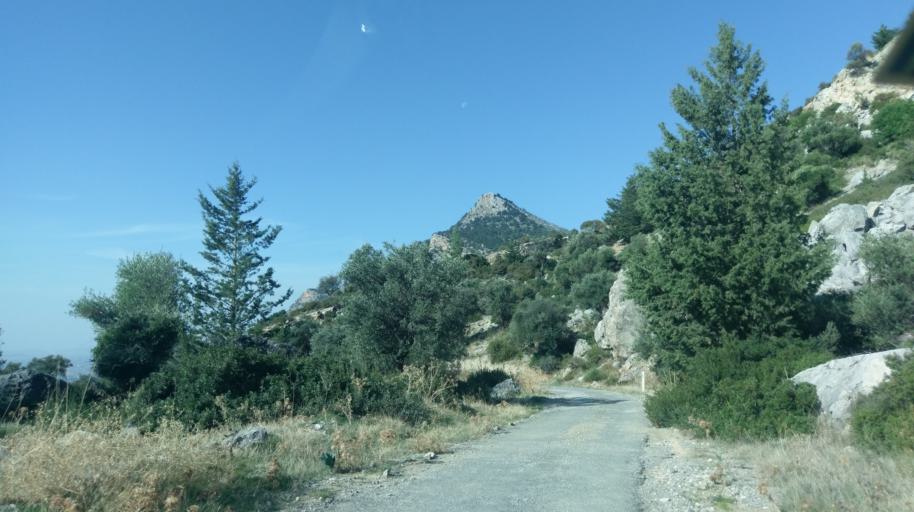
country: CY
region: Keryneia
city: Kyrenia
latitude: 35.2850
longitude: 33.3961
